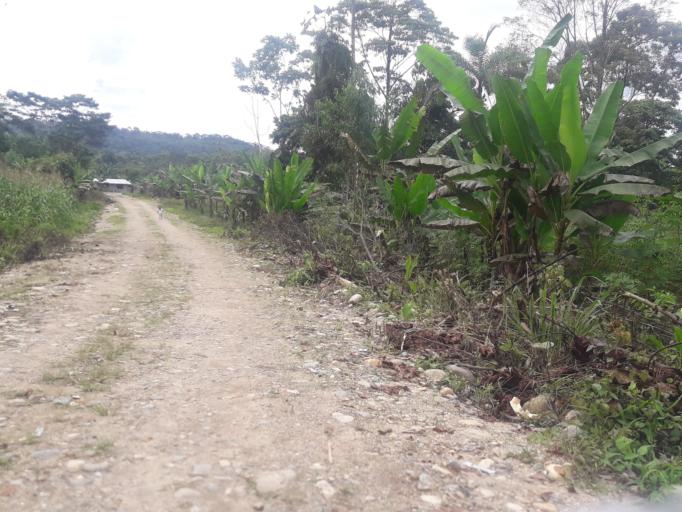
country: EC
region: Napo
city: Tena
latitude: -0.9749
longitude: -77.8503
